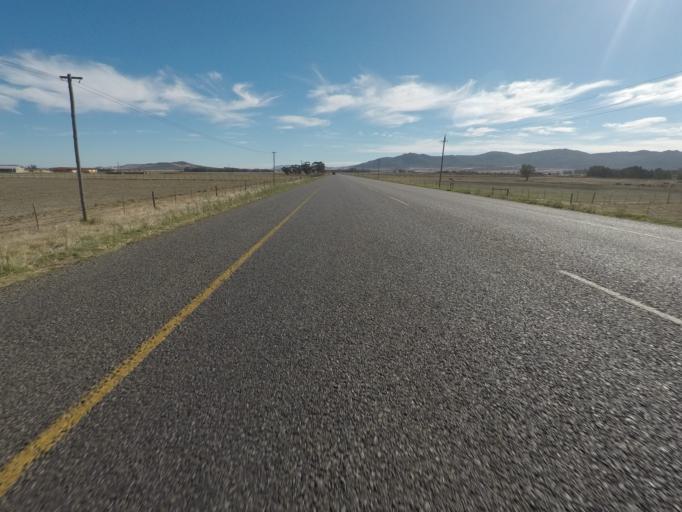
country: ZA
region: Western Cape
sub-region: West Coast District Municipality
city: Malmesbury
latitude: -33.6361
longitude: 18.7192
